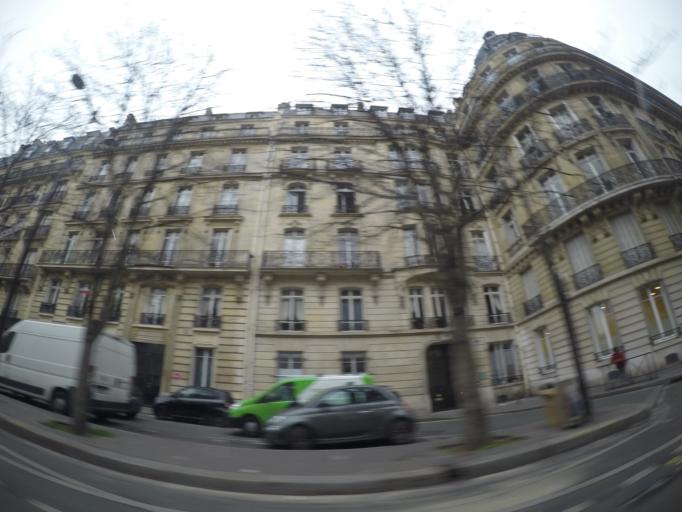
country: FR
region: Ile-de-France
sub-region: Departement des Hauts-de-Seine
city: Neuilly-sur-Seine
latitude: 48.8640
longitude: 2.2855
